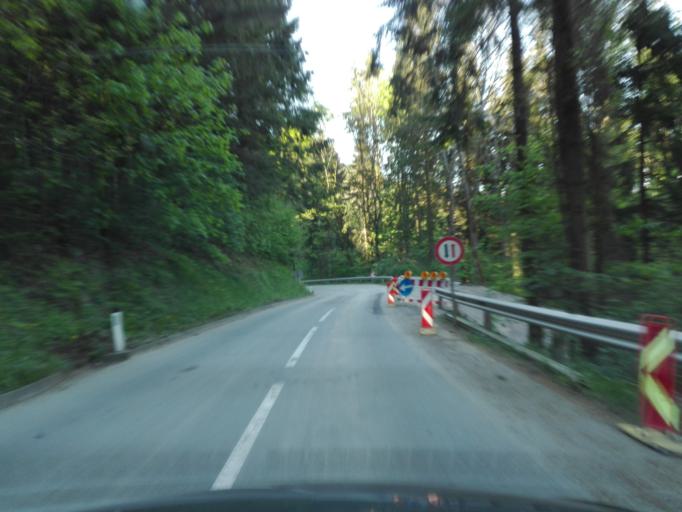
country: DE
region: Bavaria
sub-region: Lower Bavaria
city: Obernzell
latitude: 48.5320
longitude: 13.6499
